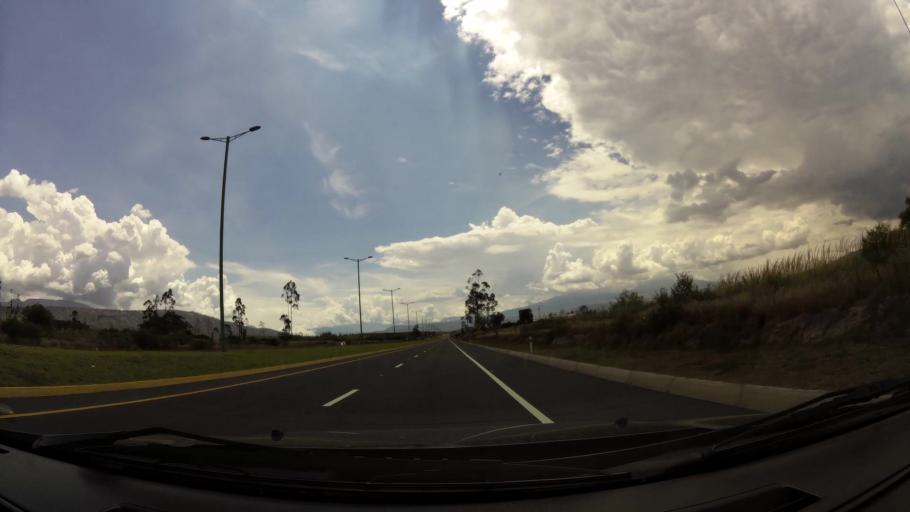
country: EC
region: Pichincha
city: Quito
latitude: -0.1237
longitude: -78.3650
